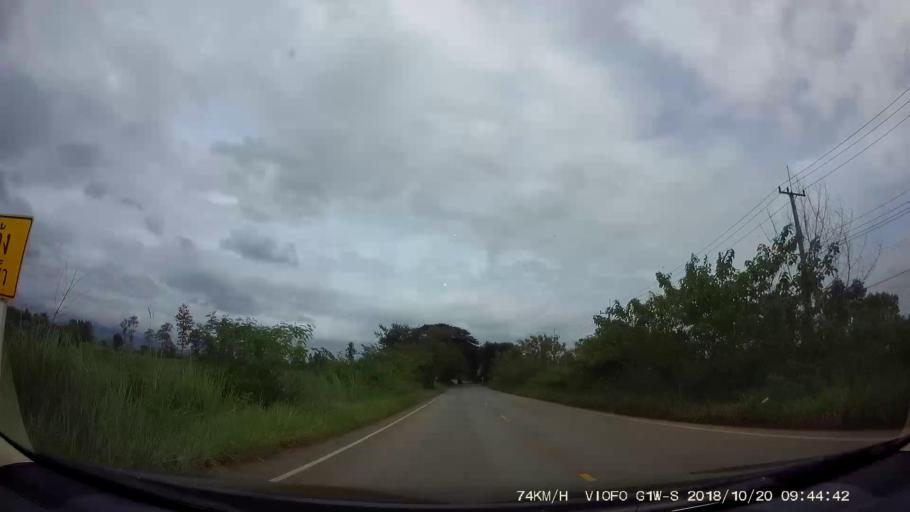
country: TH
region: Chaiyaphum
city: Khon San
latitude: 16.4859
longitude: 101.9426
